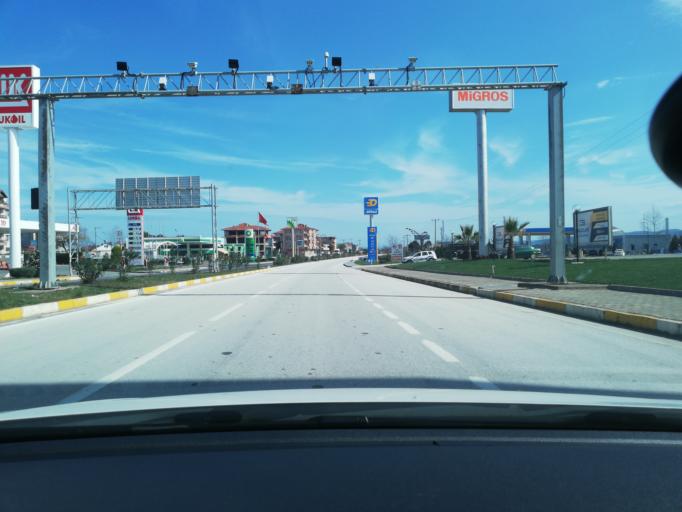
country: TR
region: Duzce
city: Akcakoca
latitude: 41.0859
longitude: 31.1769
